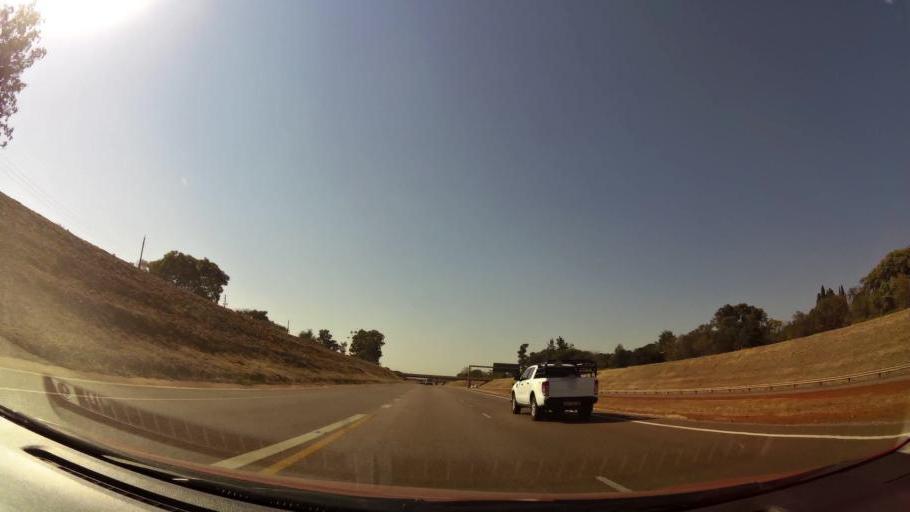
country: ZA
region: Gauteng
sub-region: City of Tshwane Metropolitan Municipality
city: Pretoria
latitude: -25.6532
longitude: 28.1279
